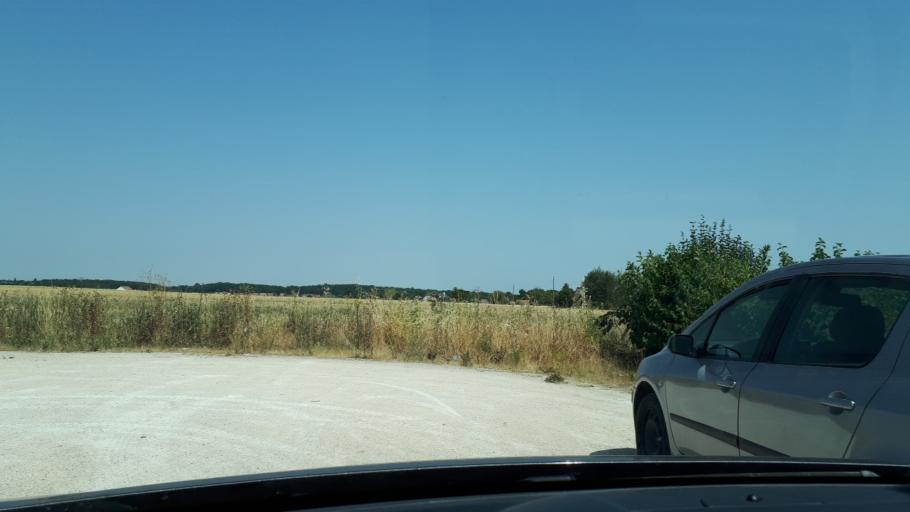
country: FR
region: Centre
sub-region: Departement du Loir-et-Cher
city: Vendome
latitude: 47.8146
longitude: 1.0518
